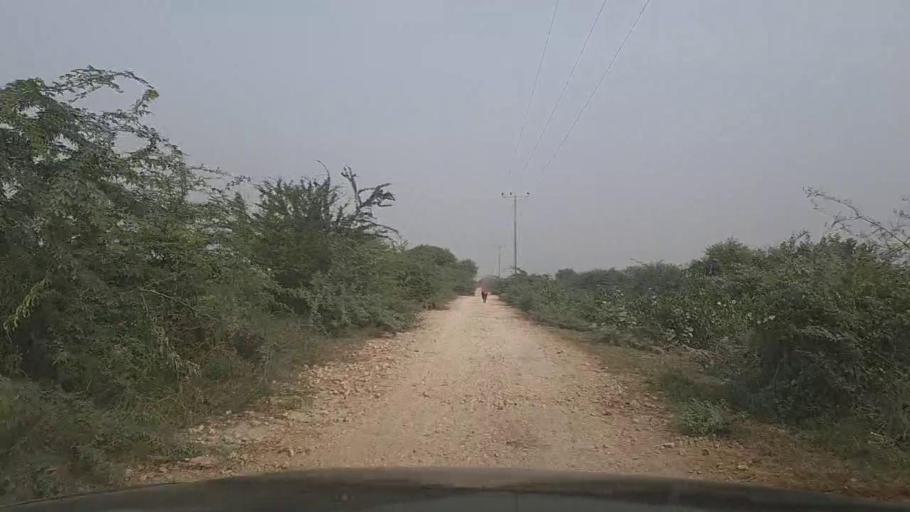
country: PK
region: Sindh
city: Mirpur Sakro
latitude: 24.5682
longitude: 67.7876
